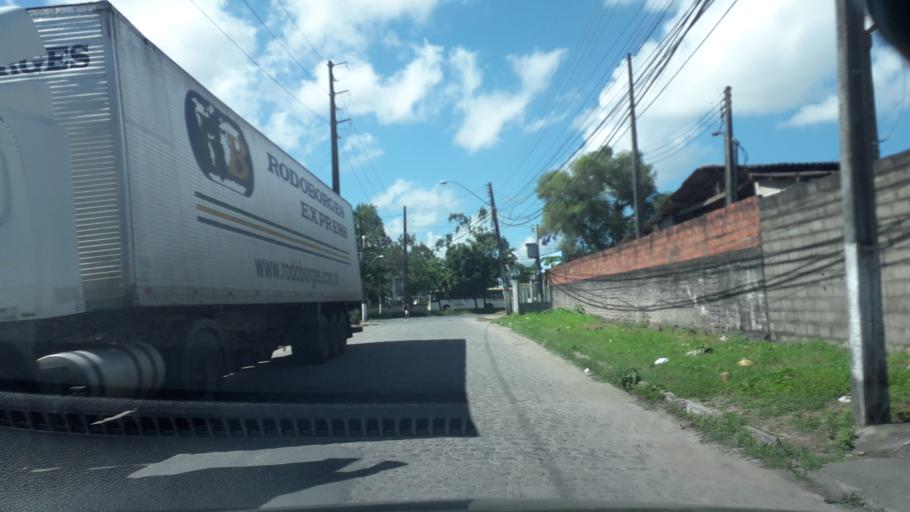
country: BR
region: Alagoas
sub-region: Satuba
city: Satuba
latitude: -9.5822
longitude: -35.7671
